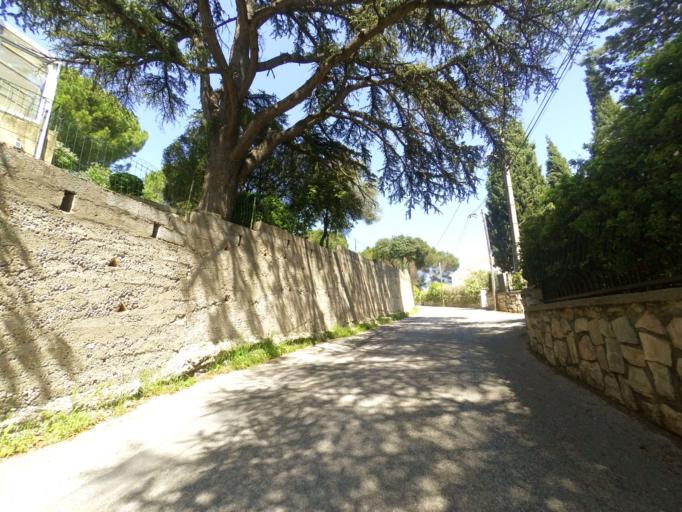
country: FR
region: Languedoc-Roussillon
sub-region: Departement du Gard
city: Calvisson
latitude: 43.7800
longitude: 4.1881
